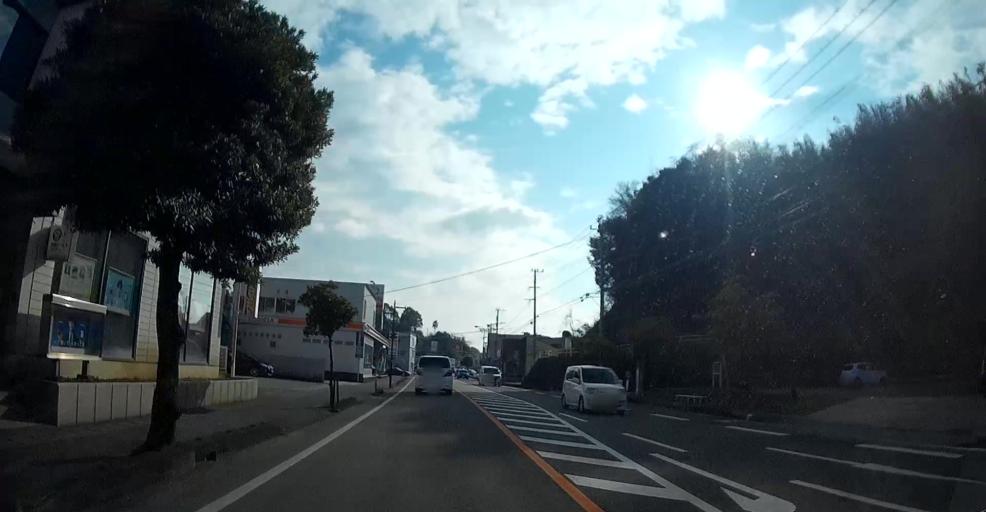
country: JP
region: Kumamoto
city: Yatsushiro
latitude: 32.5863
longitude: 130.4296
